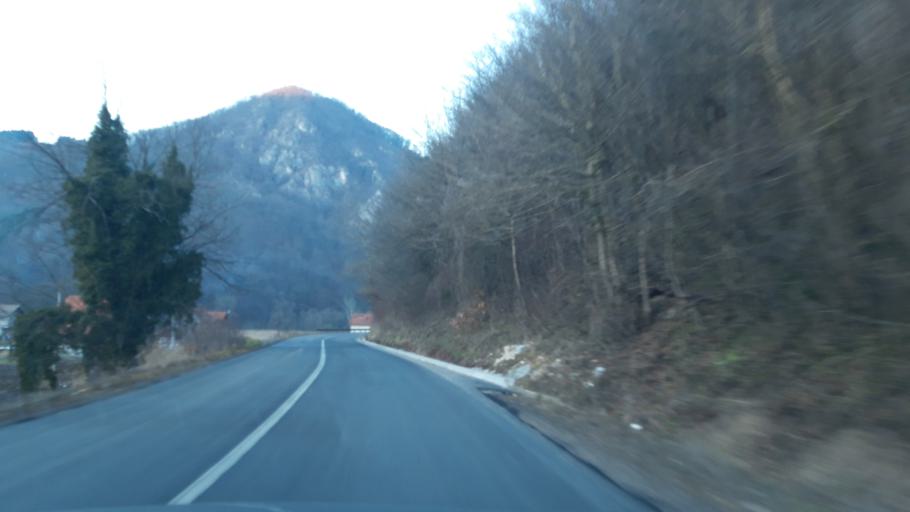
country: BA
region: Republika Srpska
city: Milici
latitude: 44.2633
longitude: 19.1038
